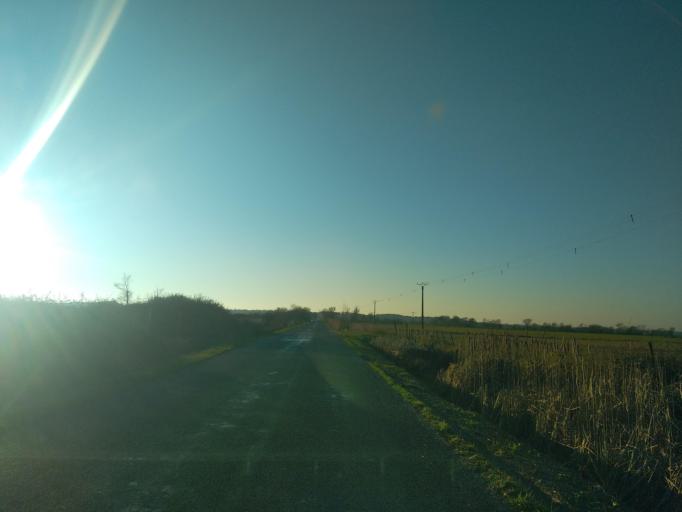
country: FR
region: Pays de la Loire
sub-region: Departement de la Vendee
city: Angles
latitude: 46.3886
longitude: -1.4454
